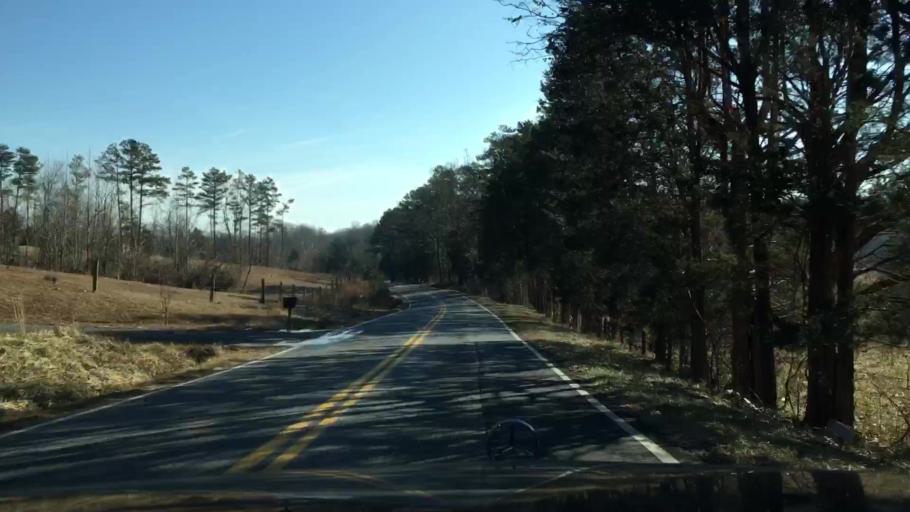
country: US
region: Virginia
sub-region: Campbell County
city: Altavista
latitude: 37.1538
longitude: -79.3590
